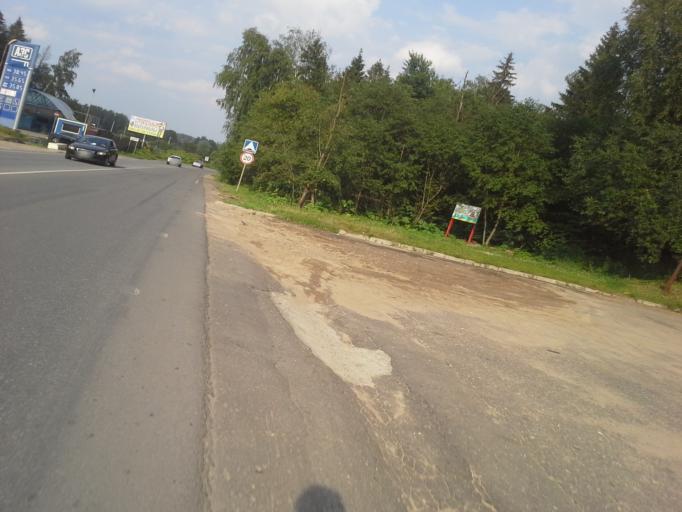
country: RU
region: Moskovskaya
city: Istra
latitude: 55.9258
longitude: 36.8871
